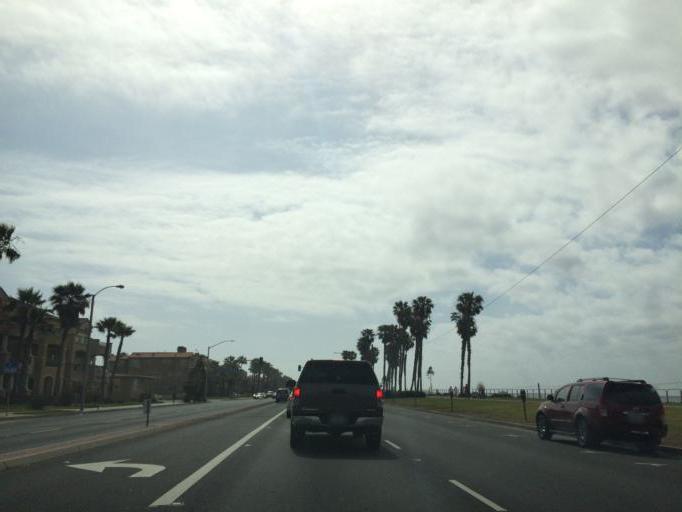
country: US
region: California
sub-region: Orange County
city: Huntington Beach
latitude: 33.6655
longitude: -118.0135
